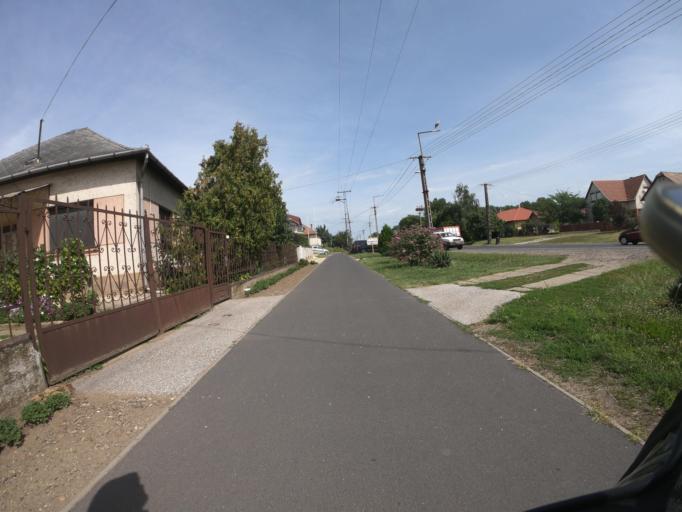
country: HU
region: Jasz-Nagykun-Szolnok
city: Tiszafured
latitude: 47.6137
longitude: 20.7491
